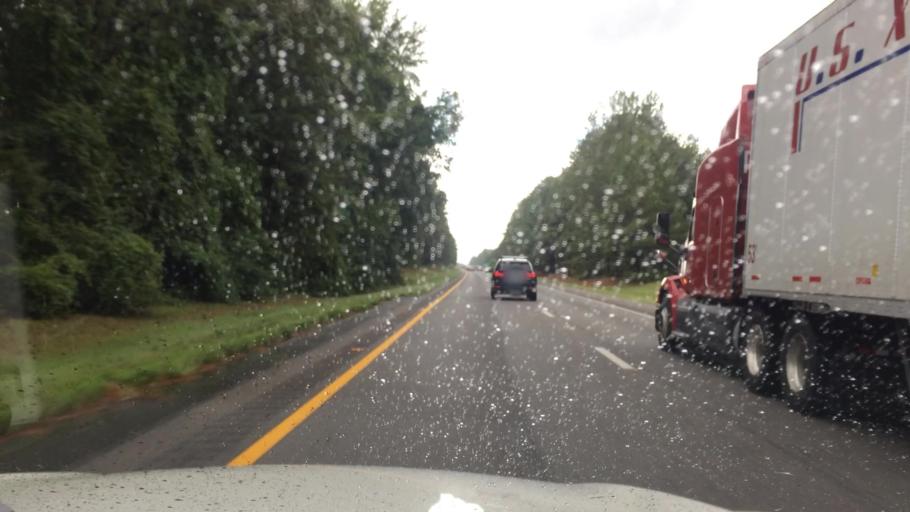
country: US
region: South Carolina
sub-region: Kershaw County
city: Elgin
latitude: 34.1500
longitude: -80.7408
